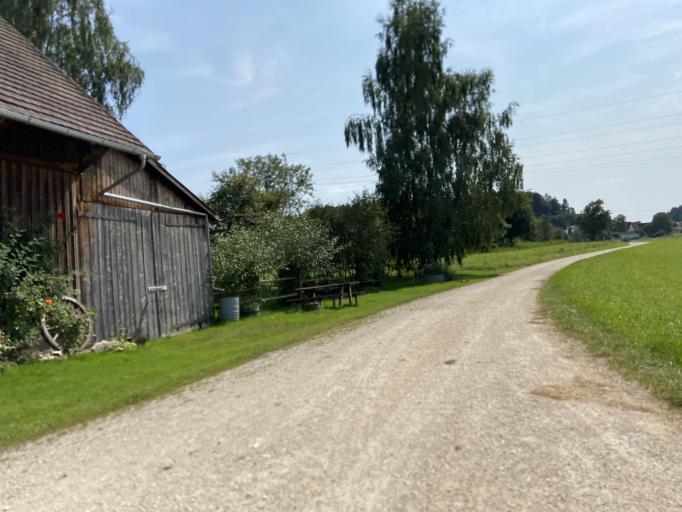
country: DE
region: Baden-Wuerttemberg
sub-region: Tuebingen Region
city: Bingen
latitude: 48.1097
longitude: 9.2932
